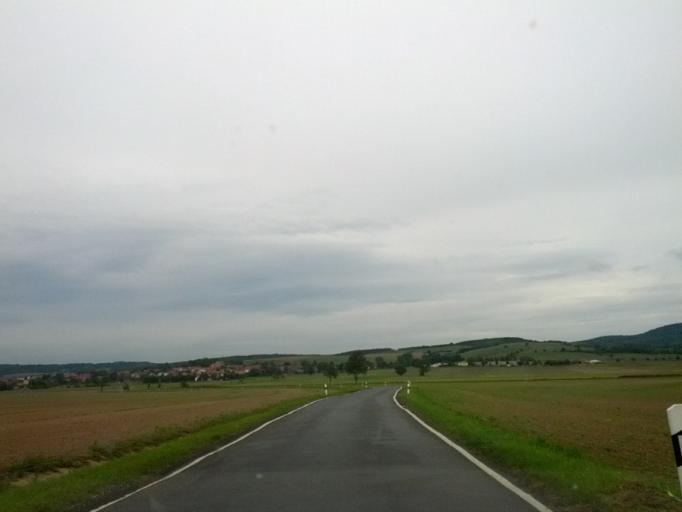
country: DE
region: Thuringia
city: Bad Salzungen
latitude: 50.8487
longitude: 10.2482
